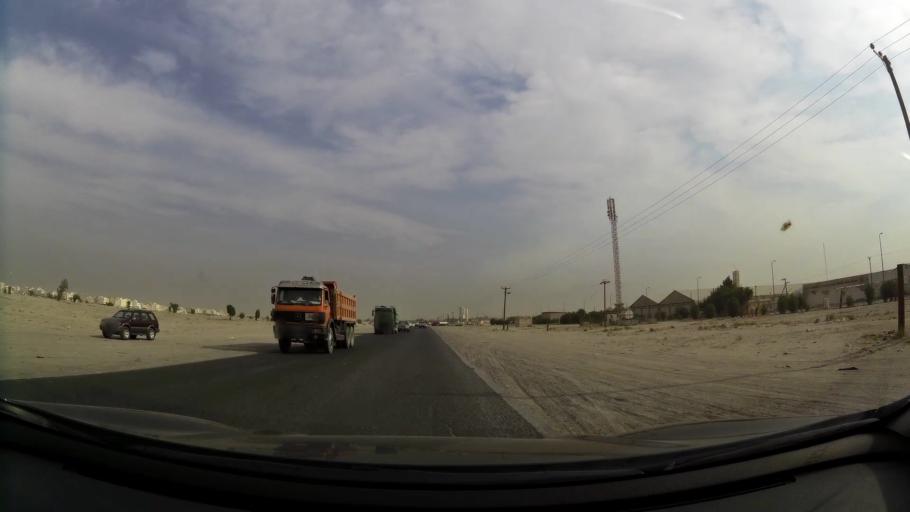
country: KW
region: Muhafazat al Jahra'
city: Al Jahra'
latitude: 29.3116
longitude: 47.7440
